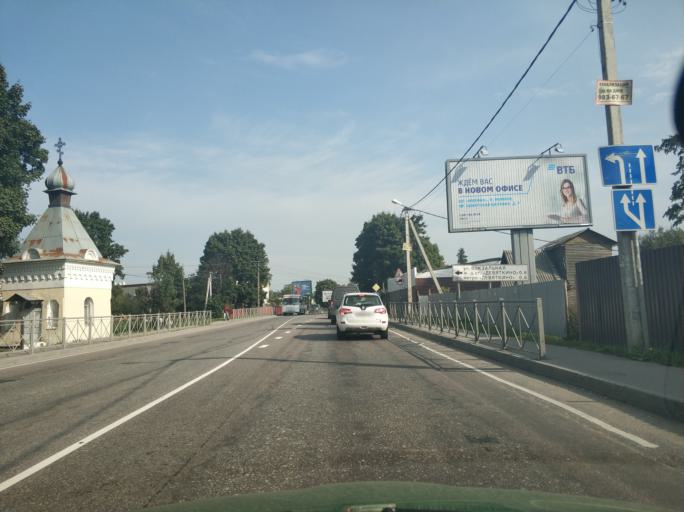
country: RU
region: Leningrad
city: Murino
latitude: 60.0444
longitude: 30.4474
